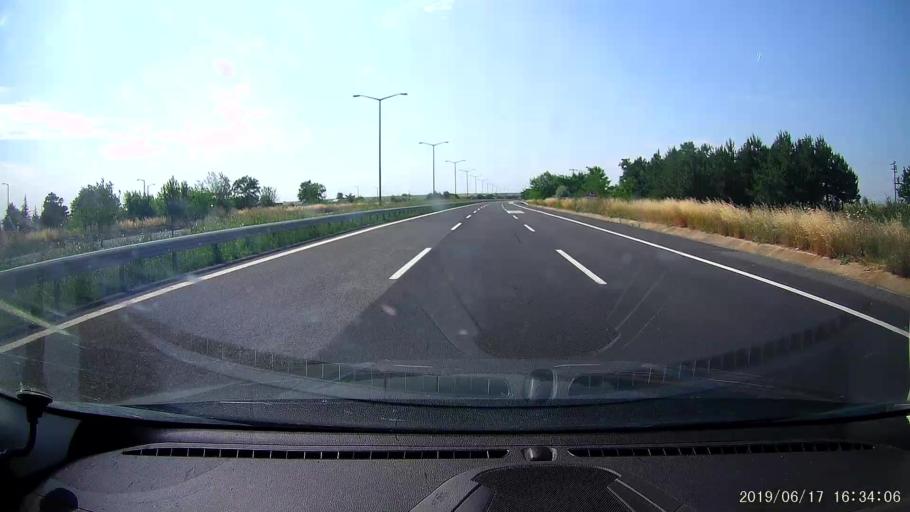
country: TR
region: Kirklareli
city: Buyukkaristiran
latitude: 41.3891
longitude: 27.5533
